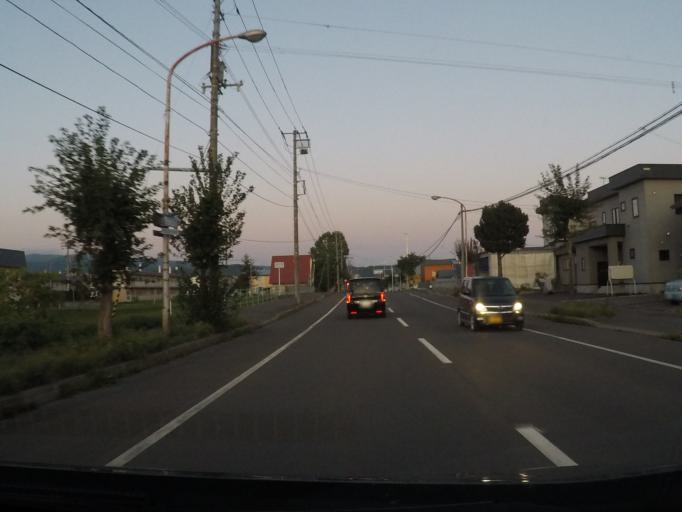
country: JP
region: Hokkaido
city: Nayoro
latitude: 44.3464
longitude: 142.4446
